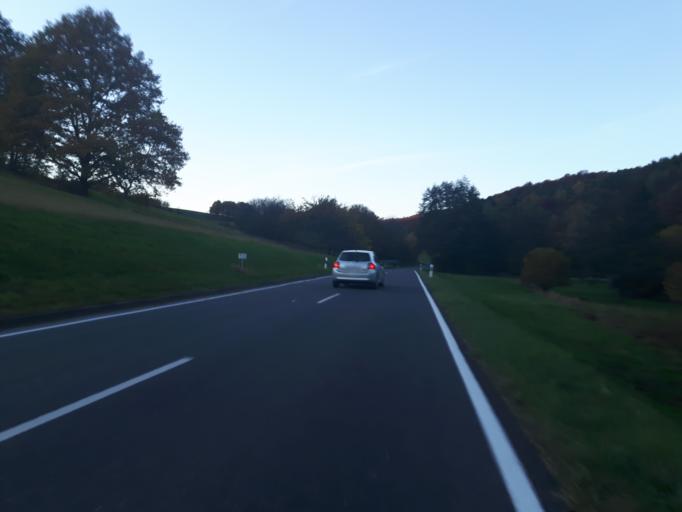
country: DE
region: Bavaria
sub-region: Regierungsbezirk Unterfranken
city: Heimbuchenthal
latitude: 49.8889
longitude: 9.2846
